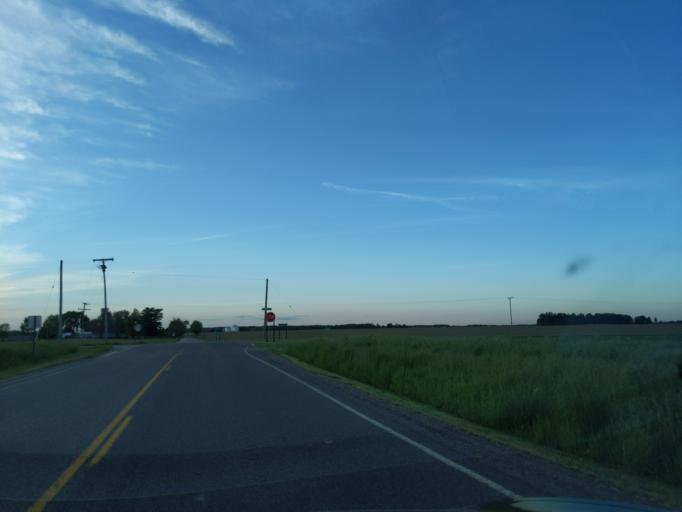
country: US
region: Michigan
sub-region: Ingham County
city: Williamston
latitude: 42.6003
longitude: -84.2989
